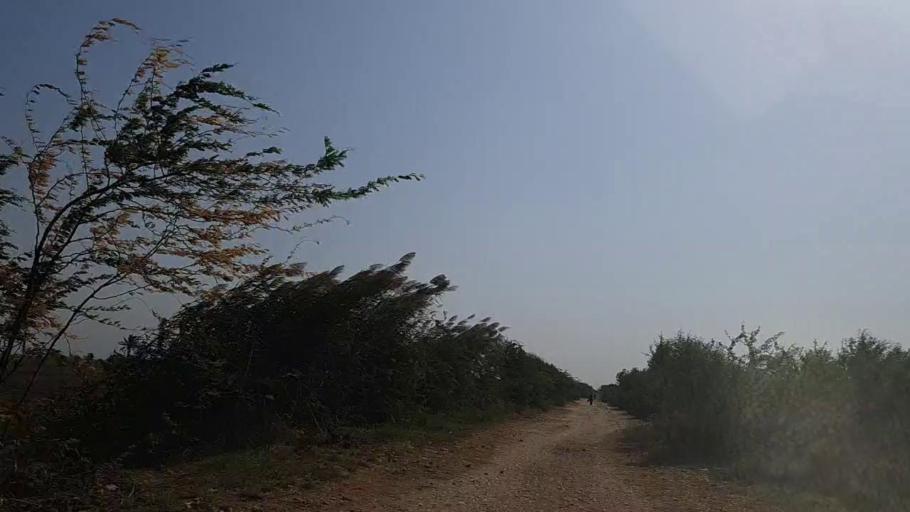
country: PK
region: Sindh
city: Daro Mehar
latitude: 24.7211
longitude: 68.0762
